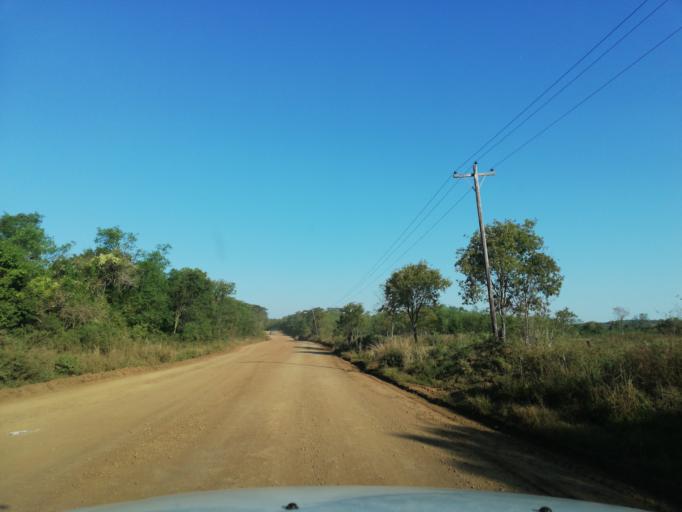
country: AR
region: Misiones
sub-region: Departamento de Candelaria
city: Candelaria
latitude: -27.5475
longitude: -55.7122
